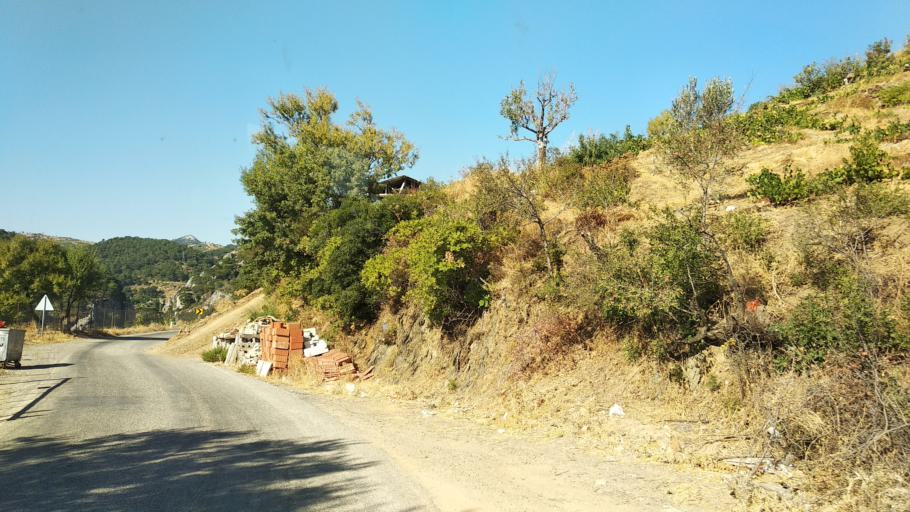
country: TR
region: Izmir
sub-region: Seferihisar
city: Seferhisar
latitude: 38.3148
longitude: 26.9553
